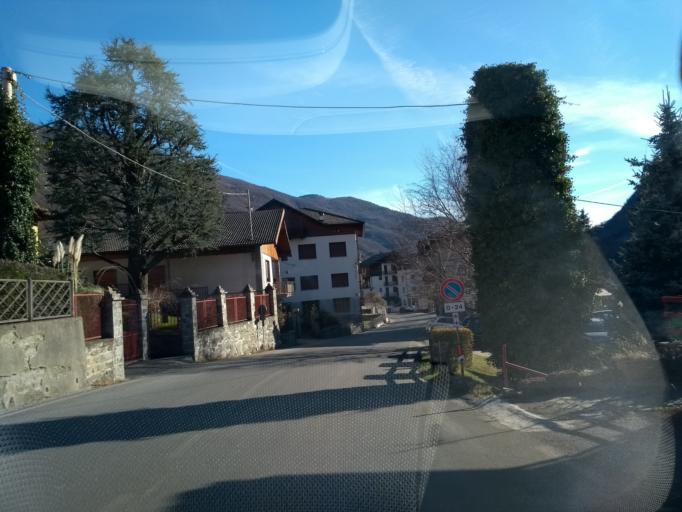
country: IT
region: Piedmont
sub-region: Provincia di Torino
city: Cantoira
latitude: 45.3459
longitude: 7.3753
